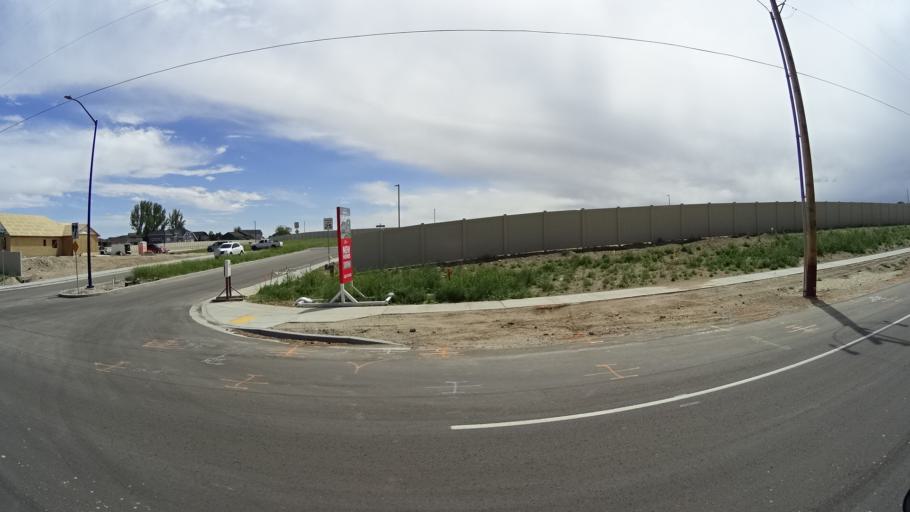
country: US
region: Idaho
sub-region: Ada County
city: Meridian
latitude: 43.5757
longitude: -116.4101
